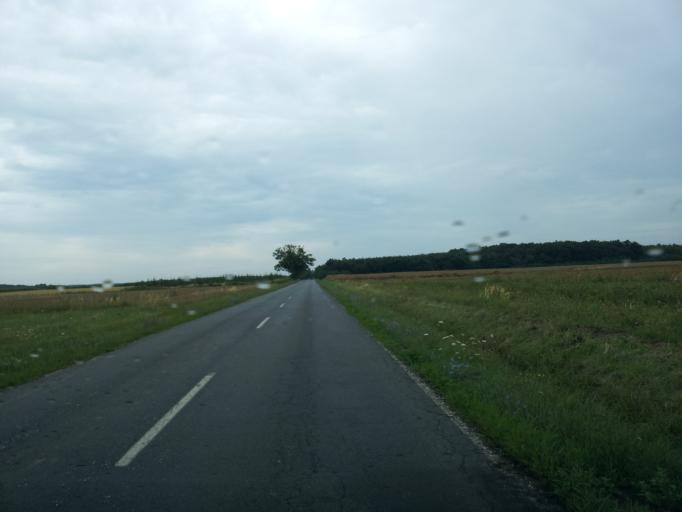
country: HU
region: Vas
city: Kormend
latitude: 46.9550
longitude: 16.6526
